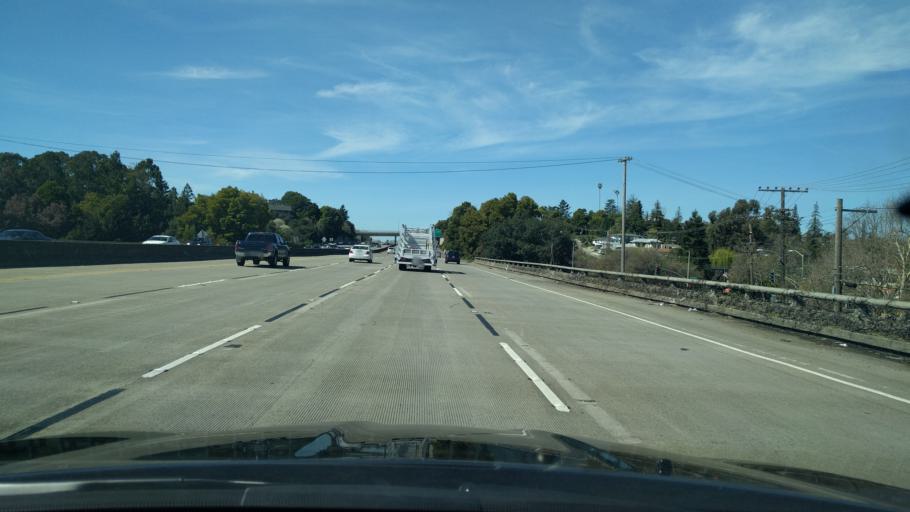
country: US
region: California
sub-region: Alameda County
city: Piedmont
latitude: 37.7982
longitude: -122.2161
